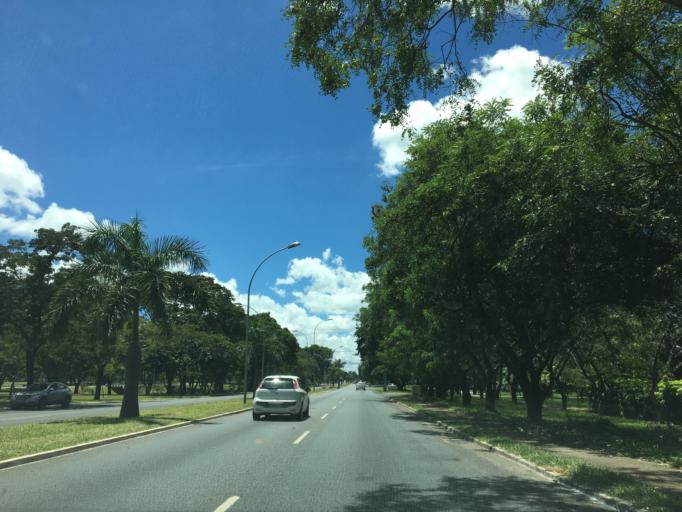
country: BR
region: Federal District
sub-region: Brasilia
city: Brasilia
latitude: -15.8266
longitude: -47.9128
